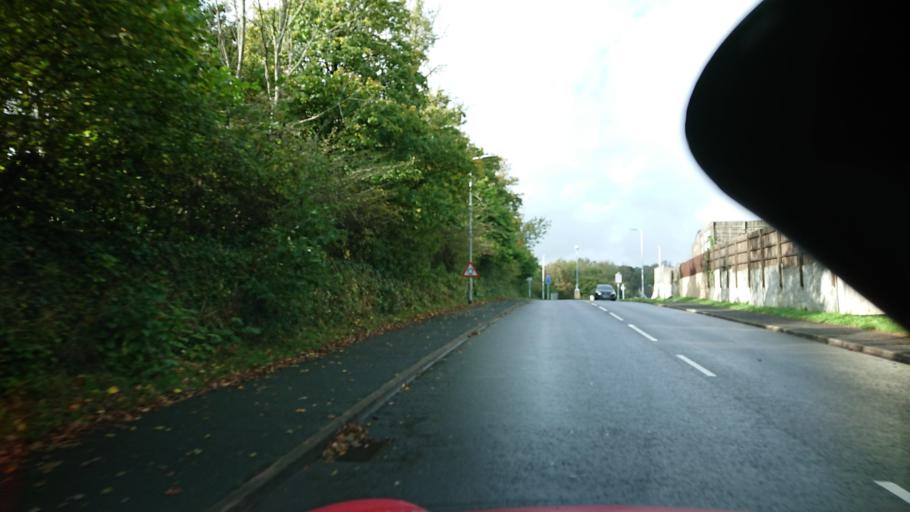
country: GB
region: England
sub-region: Plymouth
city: Plymouth
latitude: 50.3973
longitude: -4.1243
